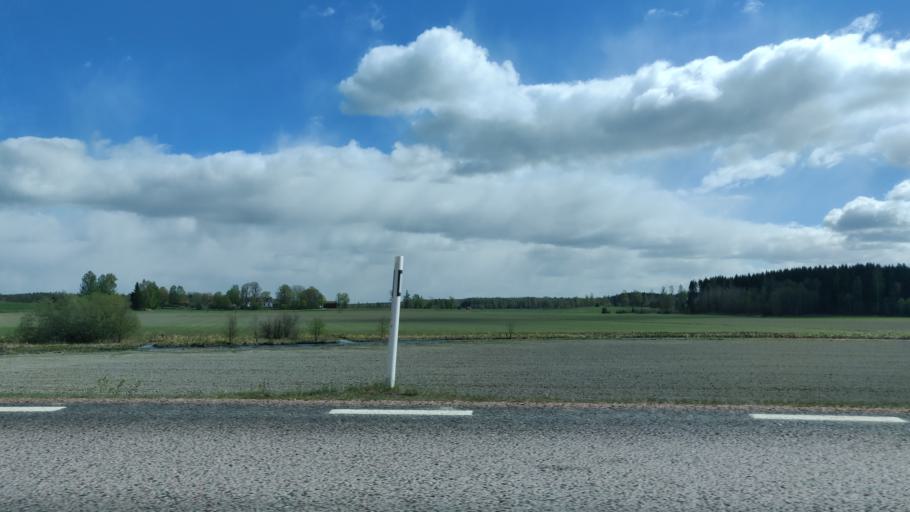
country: SE
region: Vaermland
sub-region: Karlstads Kommun
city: Skattkarr
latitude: 59.4981
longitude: 13.6129
